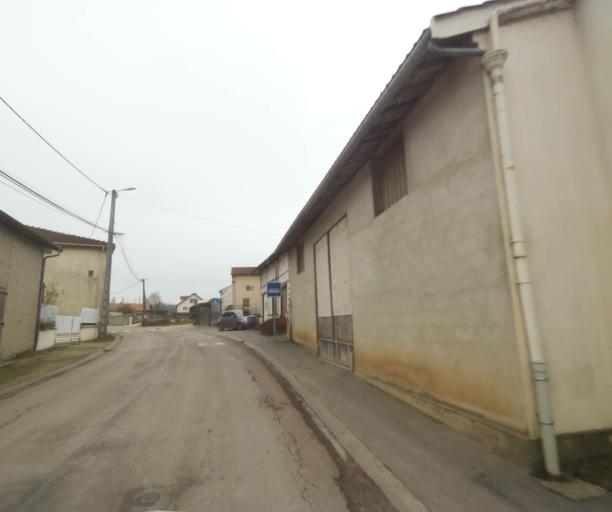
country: FR
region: Champagne-Ardenne
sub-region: Departement de la Haute-Marne
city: Wassy
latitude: 48.5433
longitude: 4.9802
